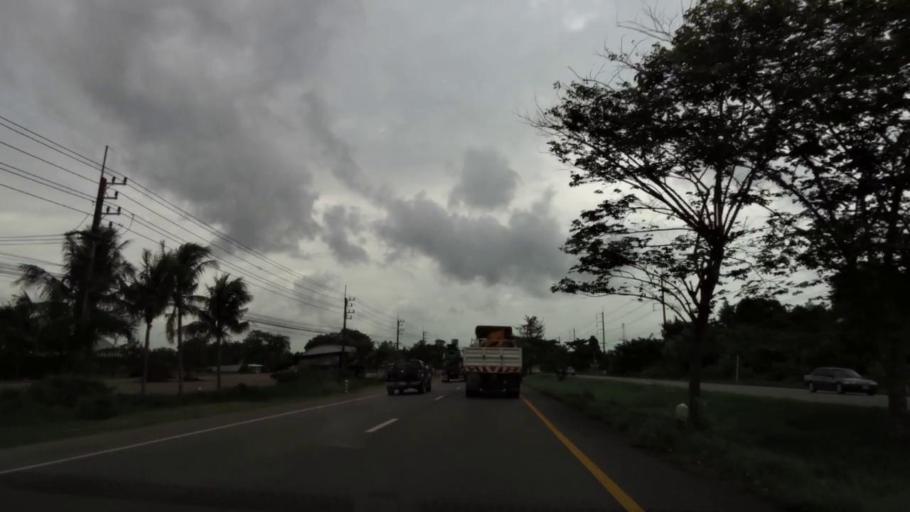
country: TH
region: Chanthaburi
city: Tha Mai
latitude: 12.7154
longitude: 101.9791
